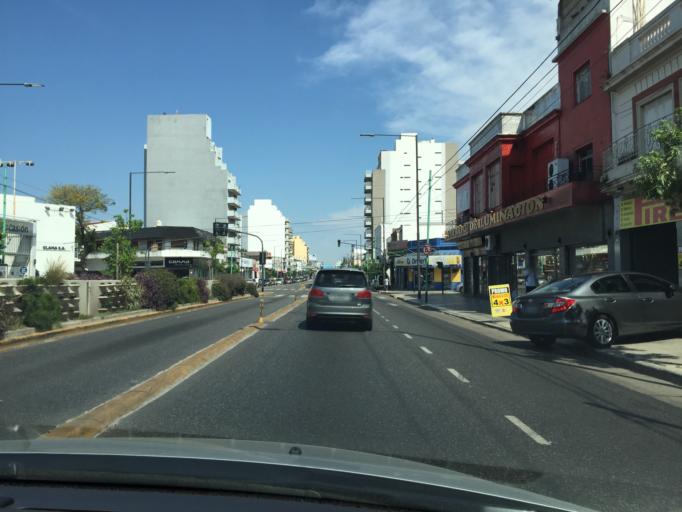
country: AR
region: Buenos Aires
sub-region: Partido de General San Martin
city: General San Martin
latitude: -34.5910
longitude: -58.5131
